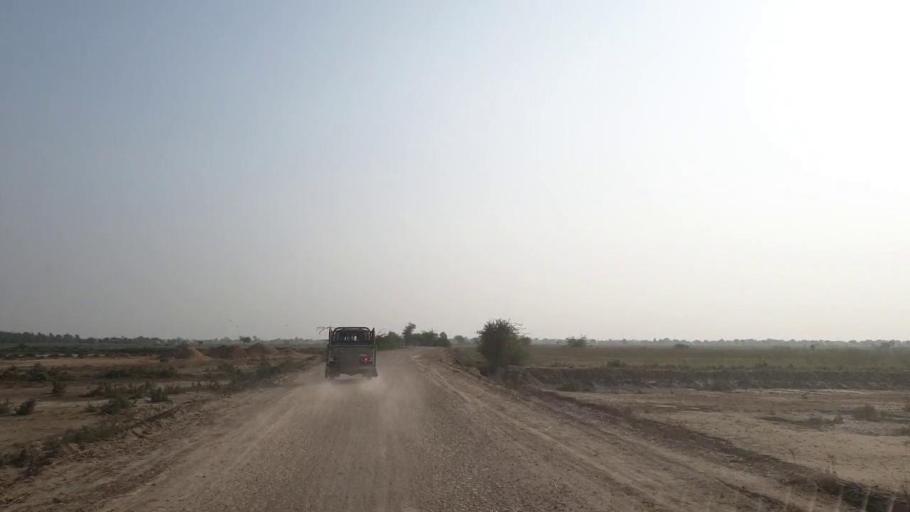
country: PK
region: Sindh
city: Kario
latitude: 24.9103
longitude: 68.5686
